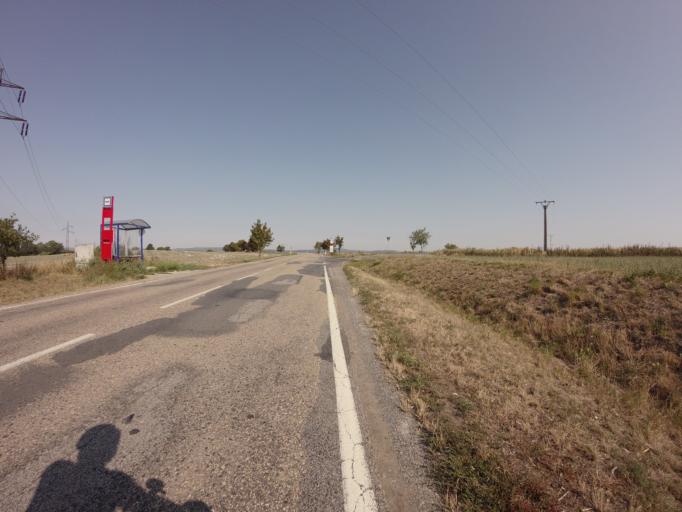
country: CZ
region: Central Bohemia
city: Porici nad Sazavou
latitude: 49.8074
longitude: 14.6498
